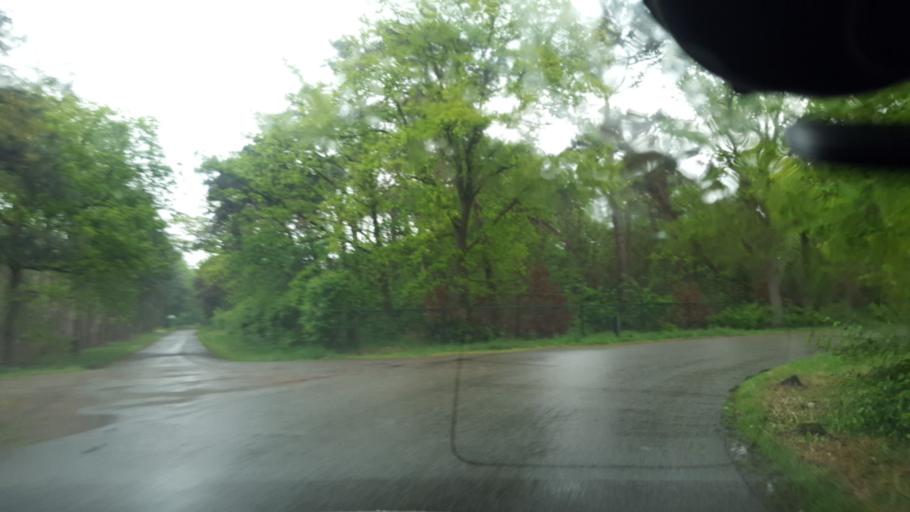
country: NL
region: North Brabant
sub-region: Gemeente Someren
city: Someren
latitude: 51.3881
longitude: 5.6669
